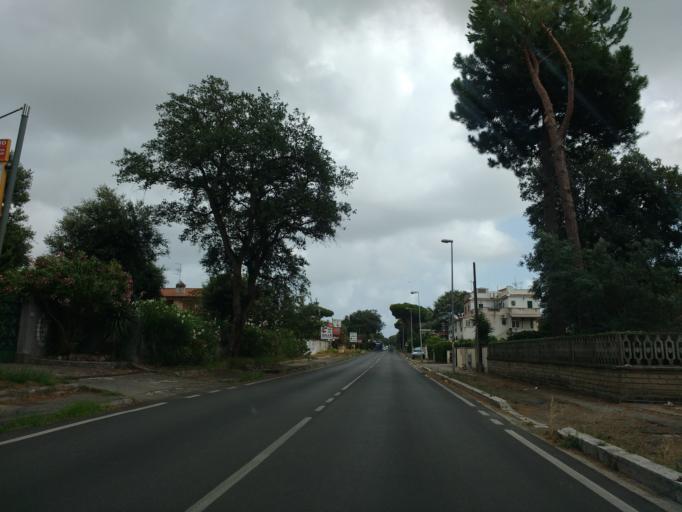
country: IT
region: Latium
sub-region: Citta metropolitana di Roma Capitale
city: Lavinio
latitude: 41.4874
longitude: 12.5990
